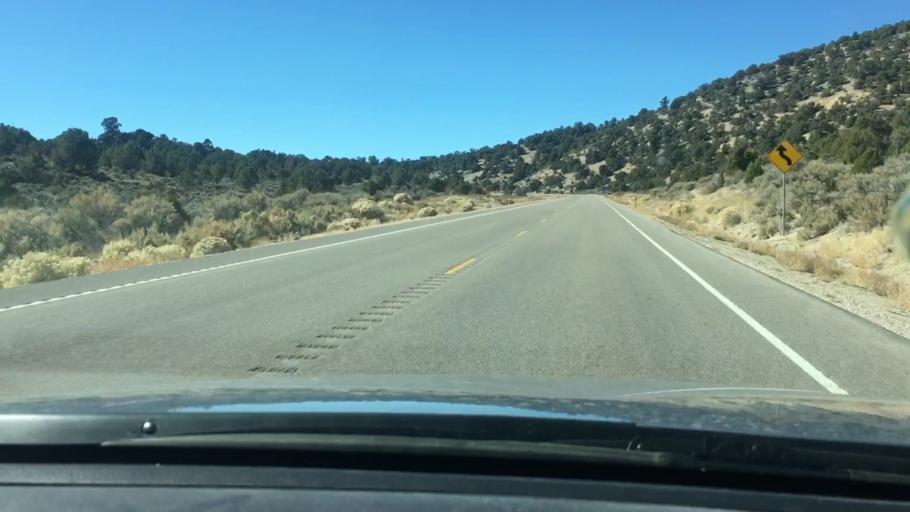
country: US
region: Nevada
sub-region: White Pine County
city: Ely
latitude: 39.2220
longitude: -114.9521
